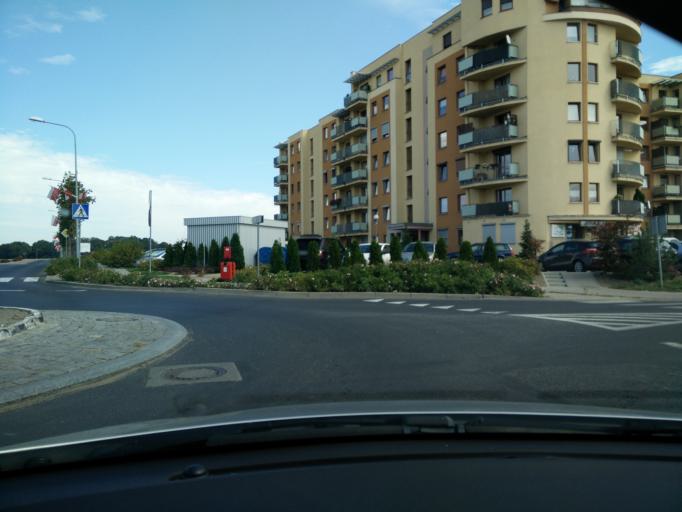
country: PL
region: Greater Poland Voivodeship
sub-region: Powiat sredzki
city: Sroda Wielkopolska
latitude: 52.2354
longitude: 17.2698
